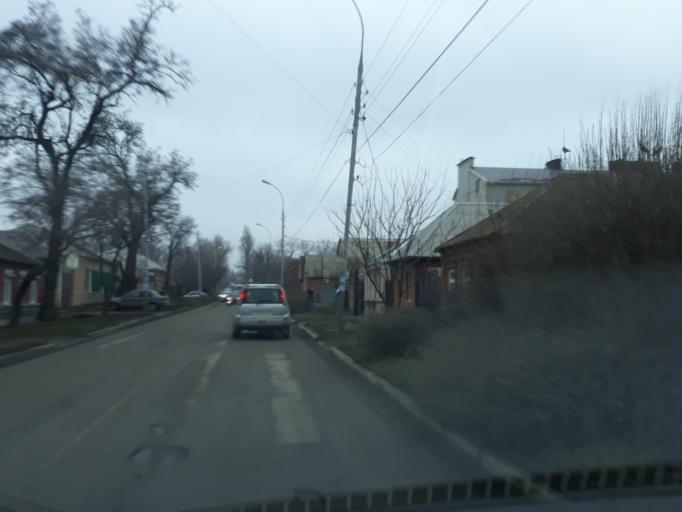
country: RU
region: Rostov
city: Taganrog
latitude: 47.2339
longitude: 38.9260
